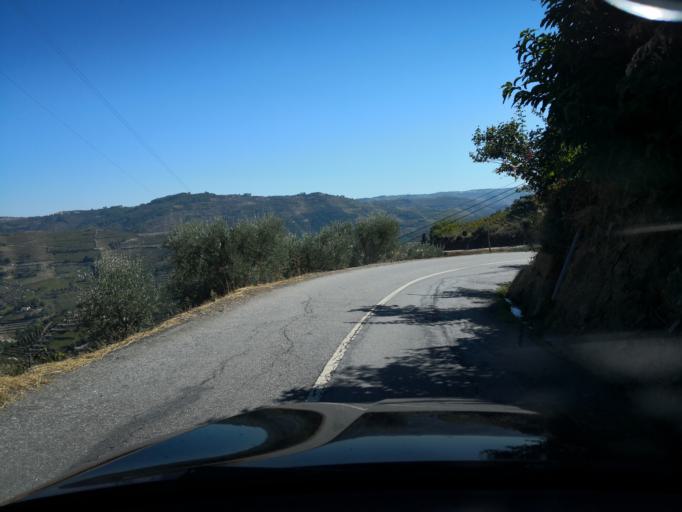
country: PT
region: Vila Real
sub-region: Santa Marta de Penaguiao
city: Santa Marta de Penaguiao
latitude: 41.2272
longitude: -7.7882
